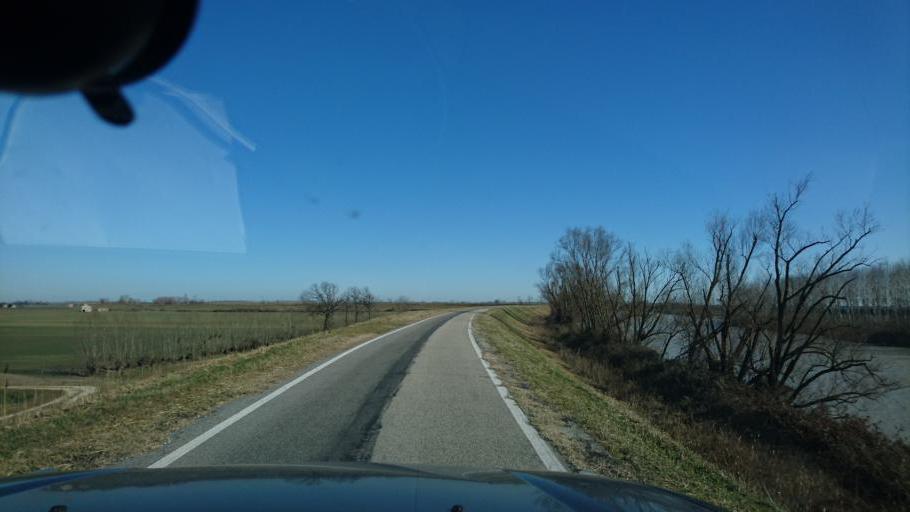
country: IT
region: Veneto
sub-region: Provincia di Rovigo
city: Ariano
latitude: 44.9315
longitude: 12.1491
